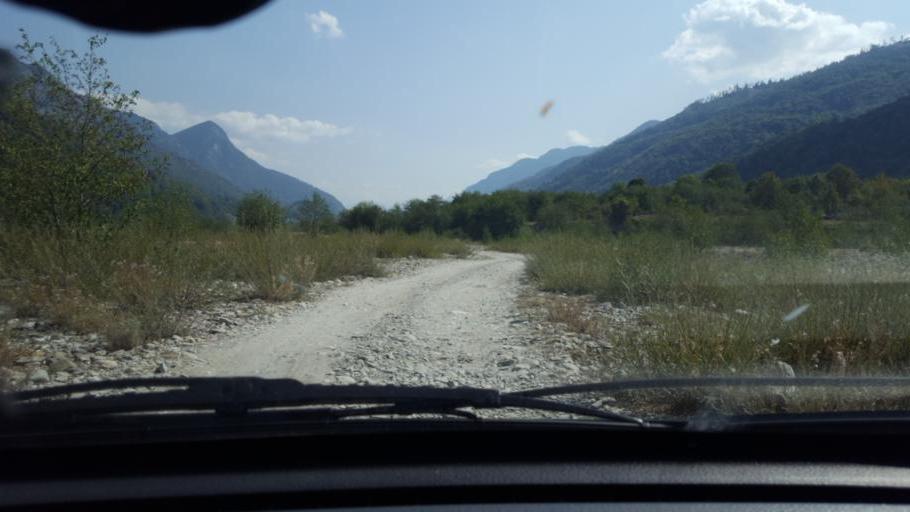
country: ME
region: Andrijevica
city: Andrijevica
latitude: 42.5940
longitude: 19.6777
